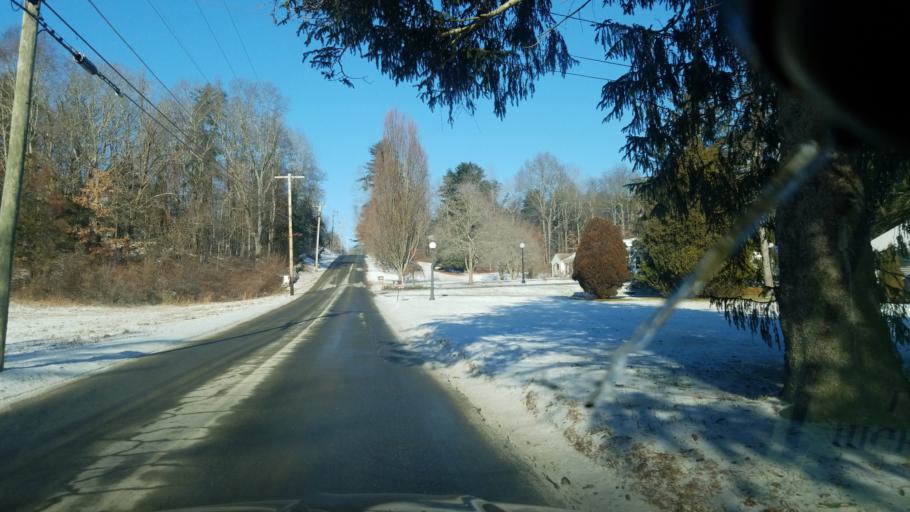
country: US
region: Connecticut
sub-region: Windham County
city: East Brooklyn
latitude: 41.8070
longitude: -71.9041
